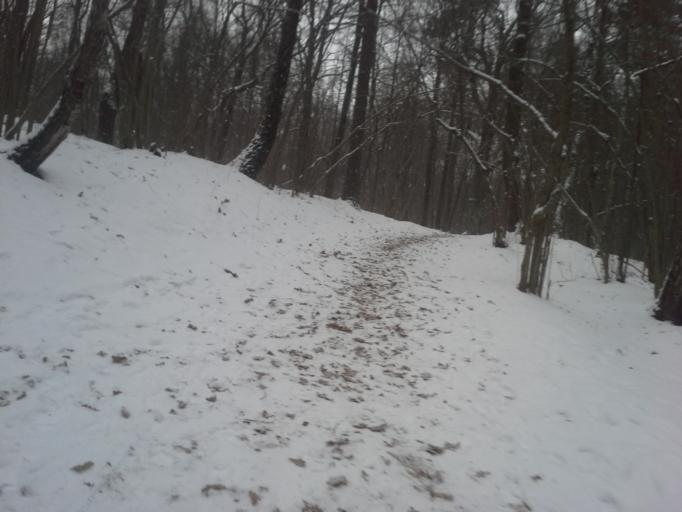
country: RU
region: Moscow
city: Chertanovo Yuzhnoye
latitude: 55.6041
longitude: 37.5630
